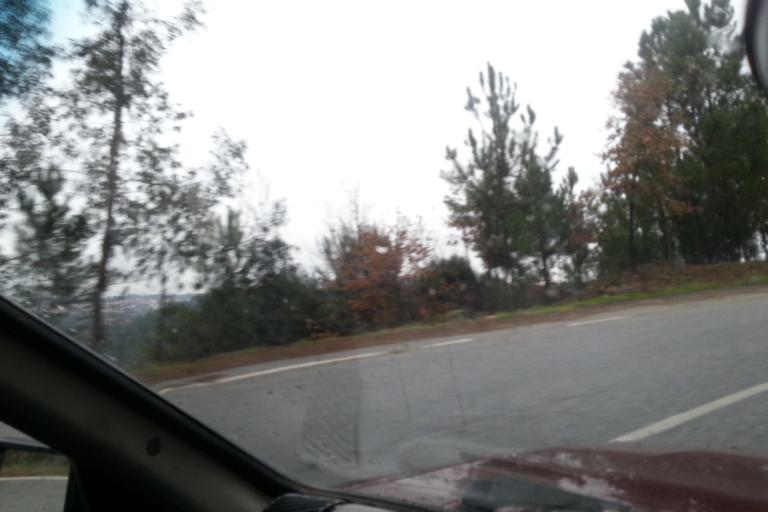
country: PT
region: Viseu
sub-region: Mangualde
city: Mangualde
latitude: 40.6334
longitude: -7.8063
